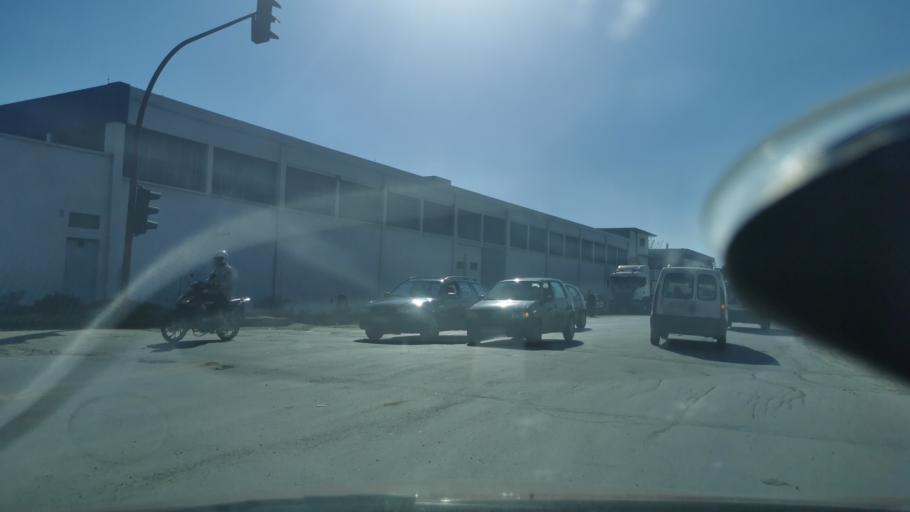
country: MA
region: Fes-Boulemane
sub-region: Fes
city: Fes
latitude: 34.0256
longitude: -4.9765
